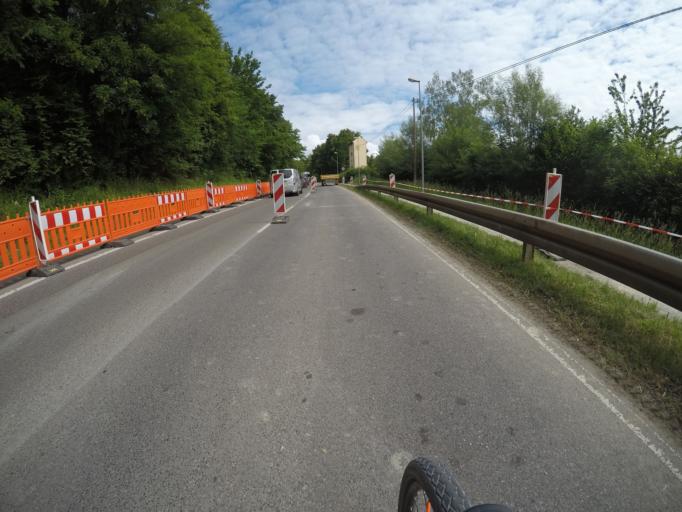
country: DE
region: Baden-Wuerttemberg
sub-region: Regierungsbezirk Stuttgart
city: Kirchheim unter Teck
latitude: 48.6579
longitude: 9.4577
